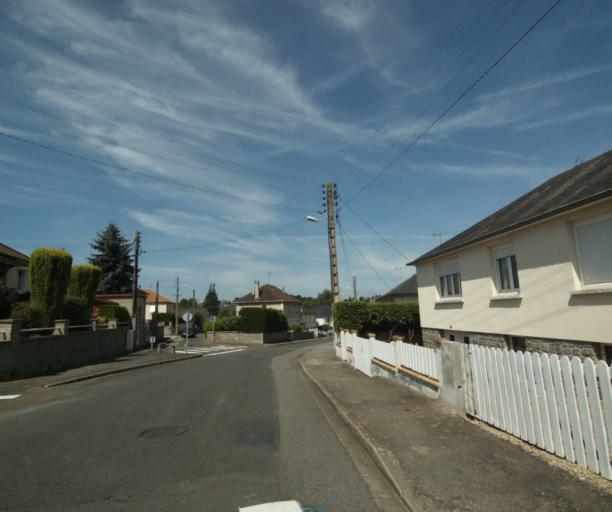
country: FR
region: Pays de la Loire
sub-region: Departement de la Mayenne
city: Laval
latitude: 48.0614
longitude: -0.7780
